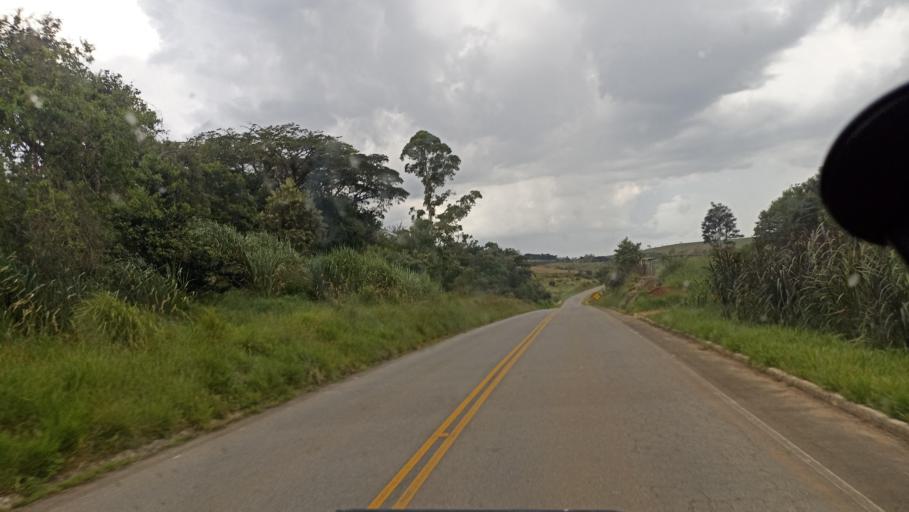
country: BR
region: Minas Gerais
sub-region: Cruzilia
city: Cruzilia
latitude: -21.9122
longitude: -44.8227
